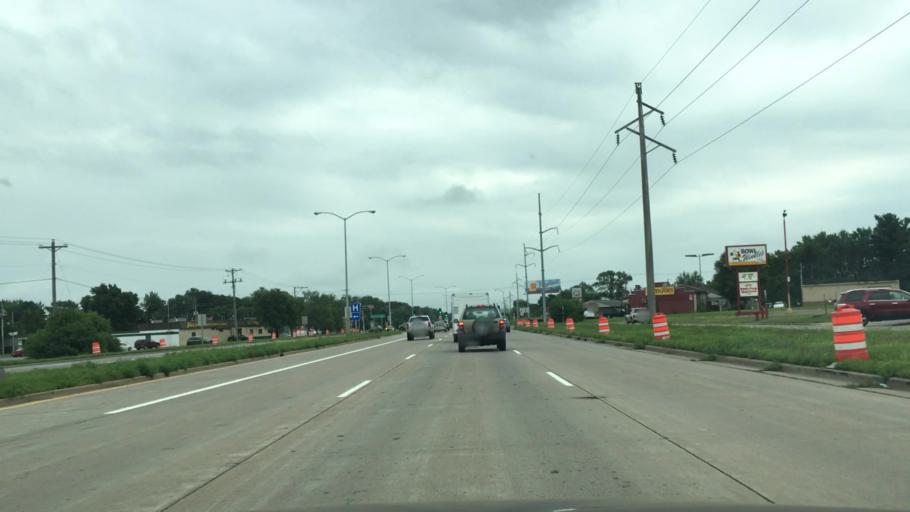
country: US
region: Wisconsin
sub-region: Eau Claire County
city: Eau Claire
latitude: 44.8161
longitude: -91.5409
